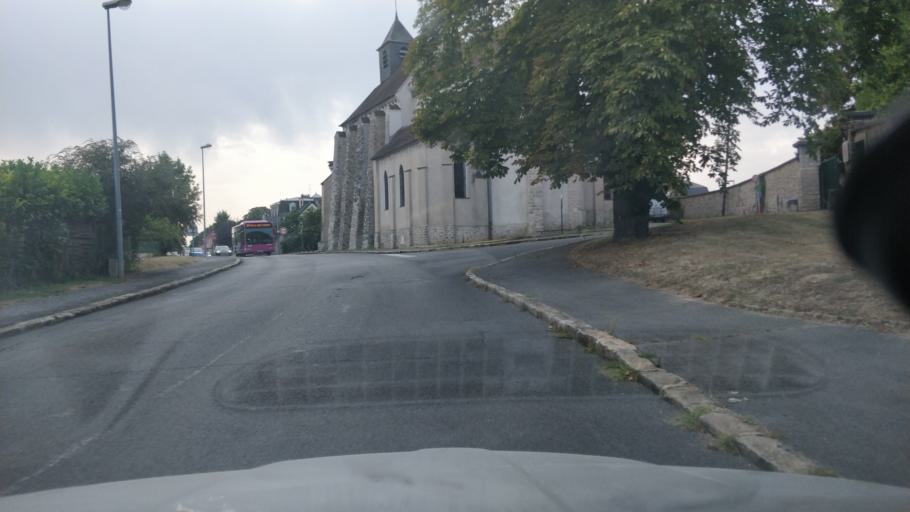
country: FR
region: Ile-de-France
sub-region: Departement de Seine-et-Marne
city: Pomponne
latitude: 48.8811
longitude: 2.6831
